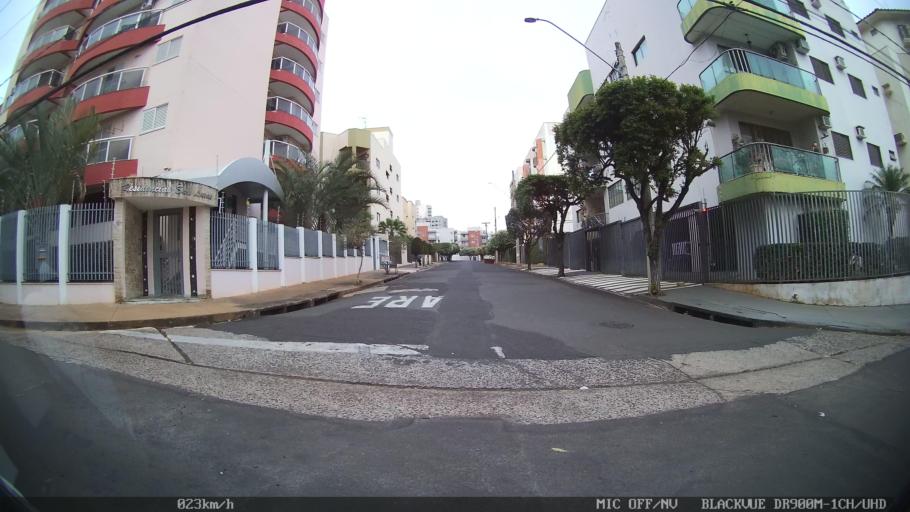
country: BR
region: Sao Paulo
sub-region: Sao Jose Do Rio Preto
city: Sao Jose do Rio Preto
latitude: -20.8304
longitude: -49.3883
